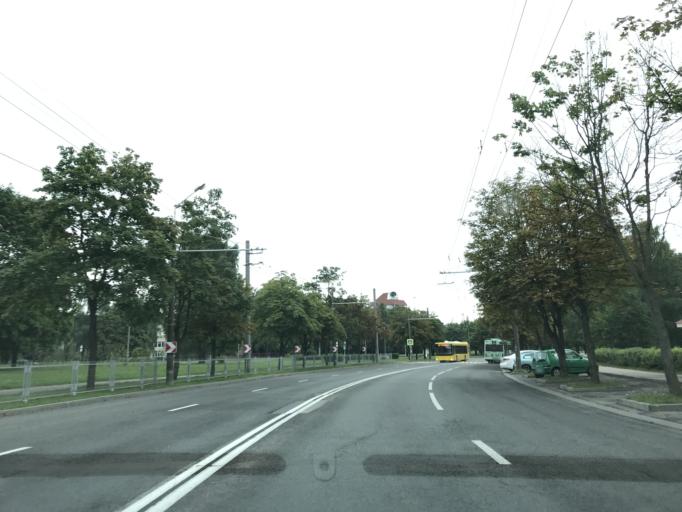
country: BY
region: Minsk
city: Borovlyany
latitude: 53.9501
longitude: 27.6395
